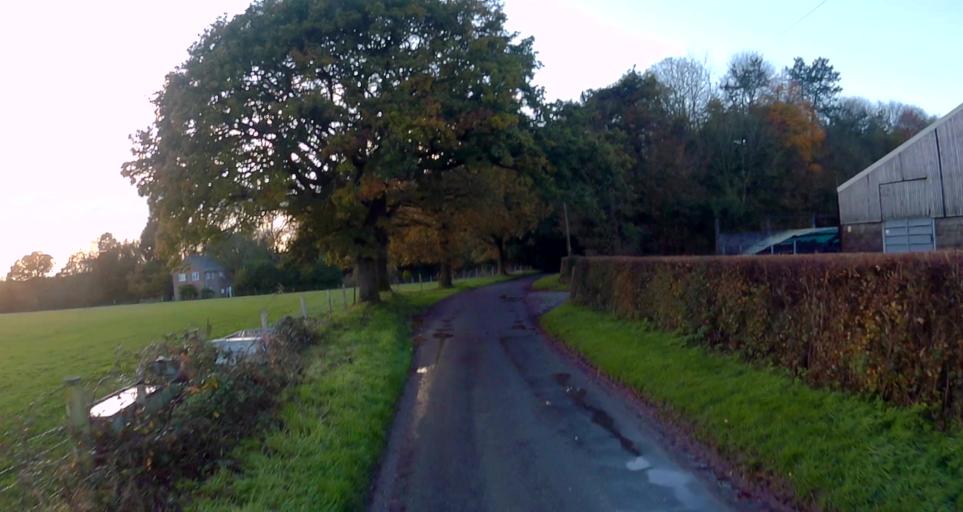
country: GB
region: England
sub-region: Hampshire
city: Basingstoke
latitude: 51.2150
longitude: -1.0996
